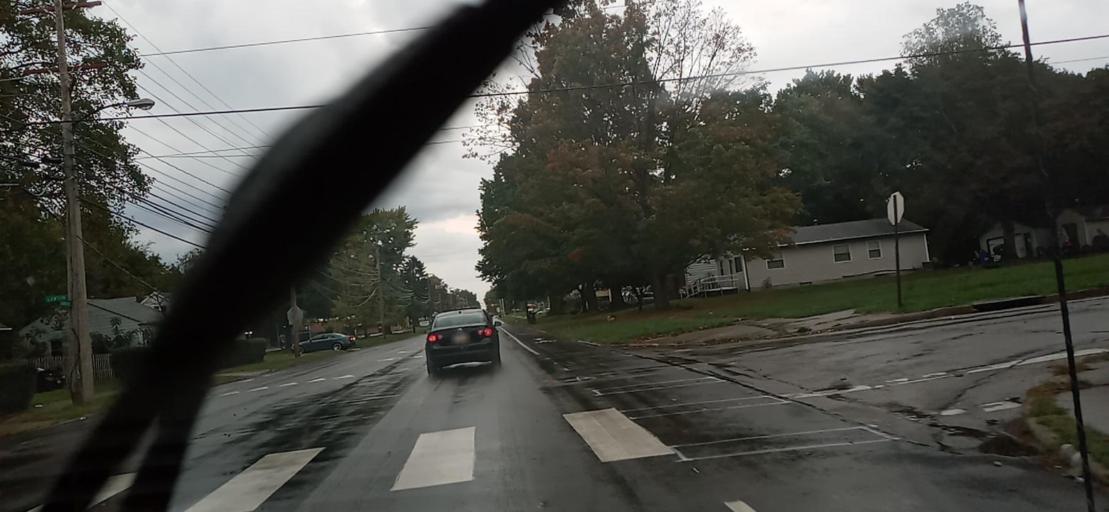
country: US
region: Ohio
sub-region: Summit County
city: Akron
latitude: 41.0796
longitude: -81.5695
